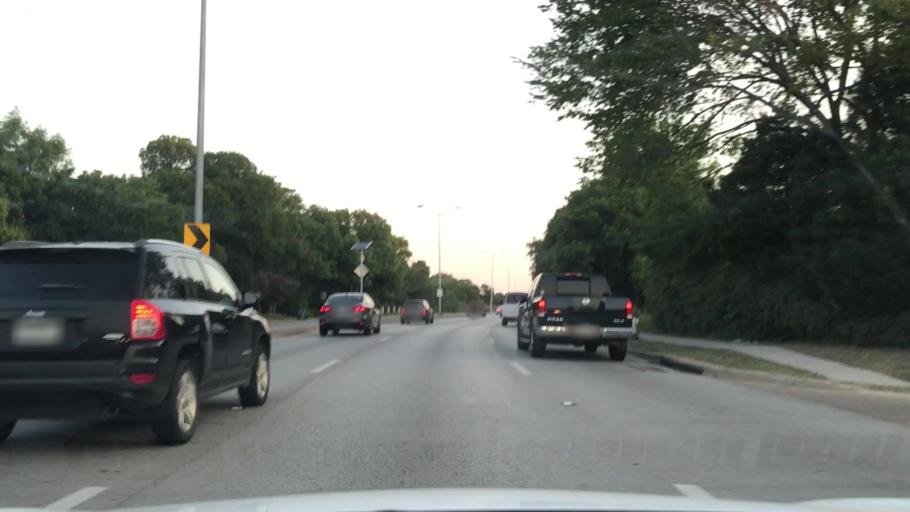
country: US
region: Texas
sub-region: Dallas County
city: Highland Park
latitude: 32.8255
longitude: -96.6969
